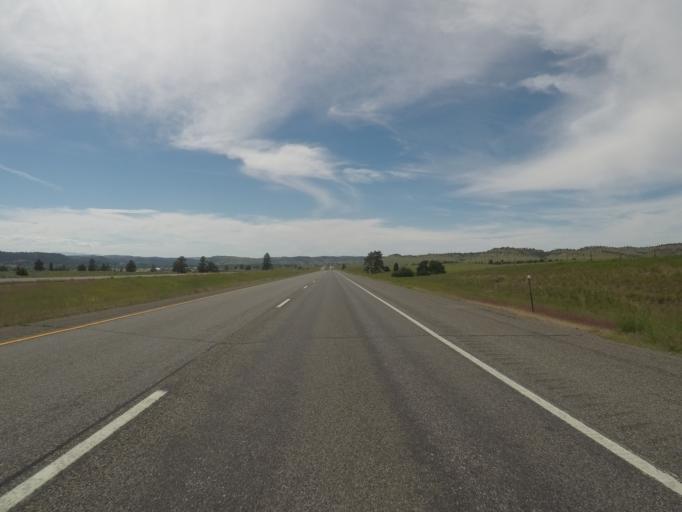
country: US
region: Montana
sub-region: Stillwater County
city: Columbus
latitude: 45.6333
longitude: -109.2075
